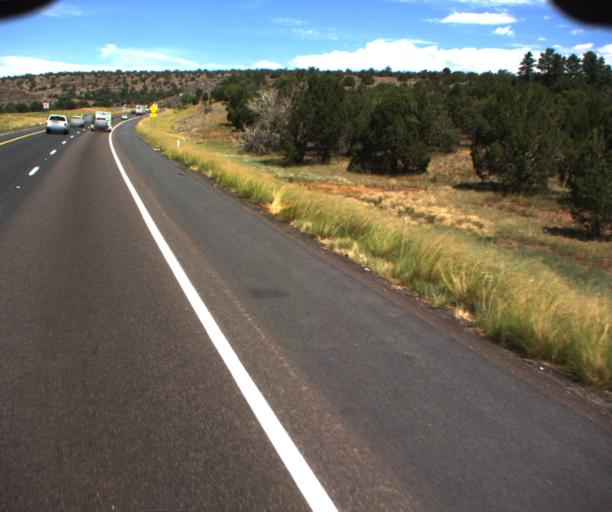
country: US
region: Arizona
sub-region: Yavapai County
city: Village of Oak Creek (Big Park)
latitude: 34.8031
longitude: -111.5965
